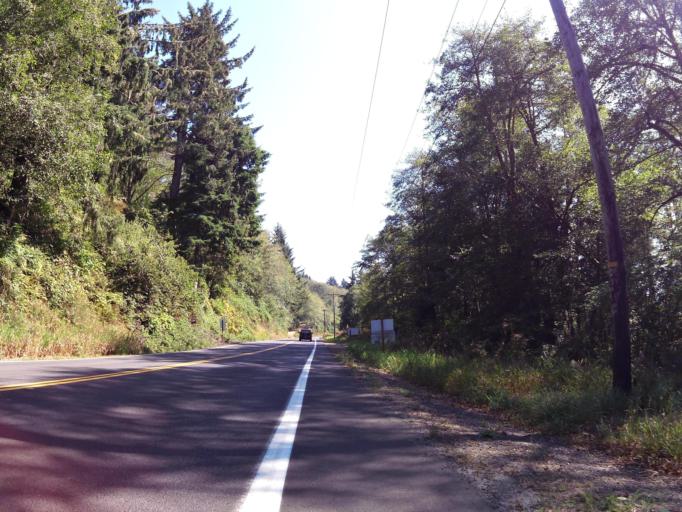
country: US
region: Oregon
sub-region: Tillamook County
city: Pacific City
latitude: 45.1904
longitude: -123.9514
